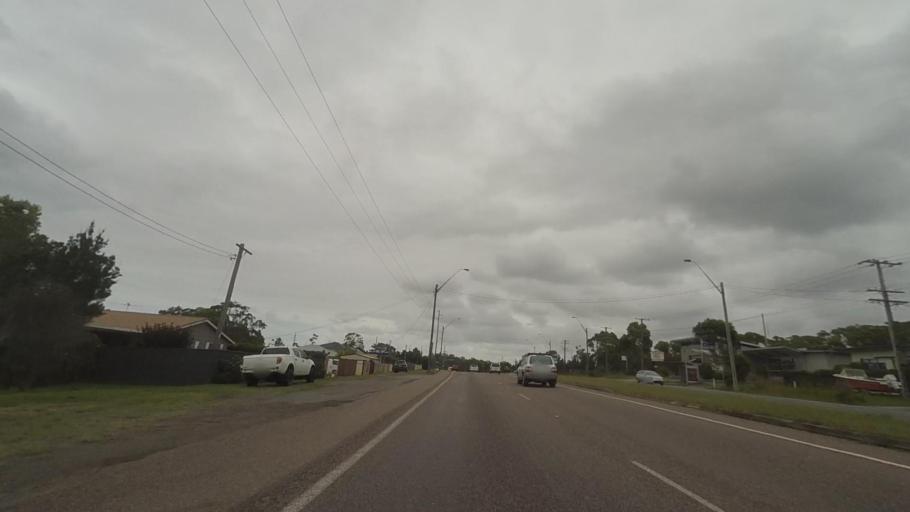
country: AU
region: New South Wales
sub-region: Wyong Shire
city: Buff Point
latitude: -33.1981
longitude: 151.5241
